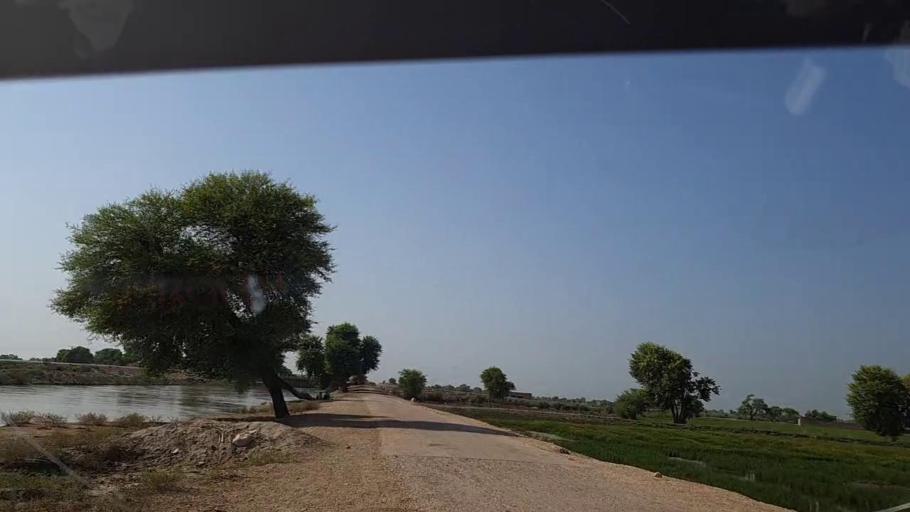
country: PK
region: Sindh
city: Ghauspur
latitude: 28.1995
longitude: 69.0428
